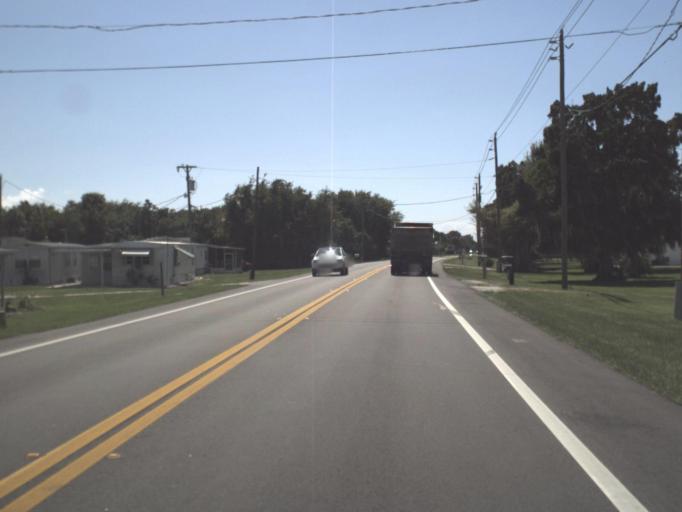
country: US
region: Florida
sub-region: Glades County
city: Buckhead Ridge
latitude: 27.1737
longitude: -80.8560
